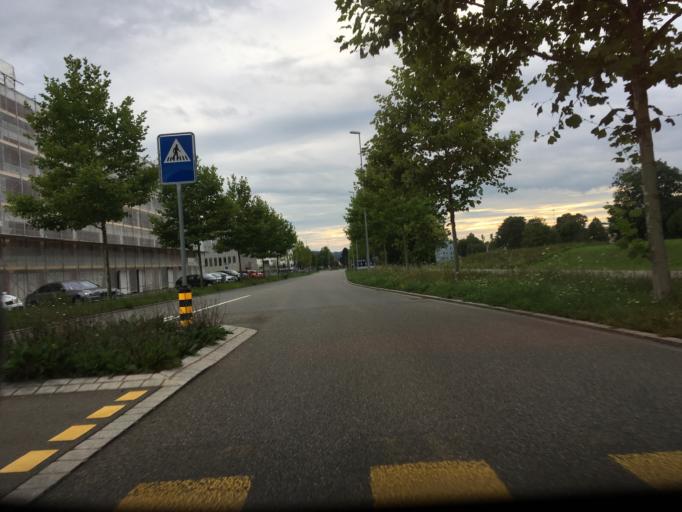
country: CH
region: Zurich
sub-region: Bezirk Uster
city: Volketswil / Volketswil (Dorf)
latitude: 47.3896
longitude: 8.6865
